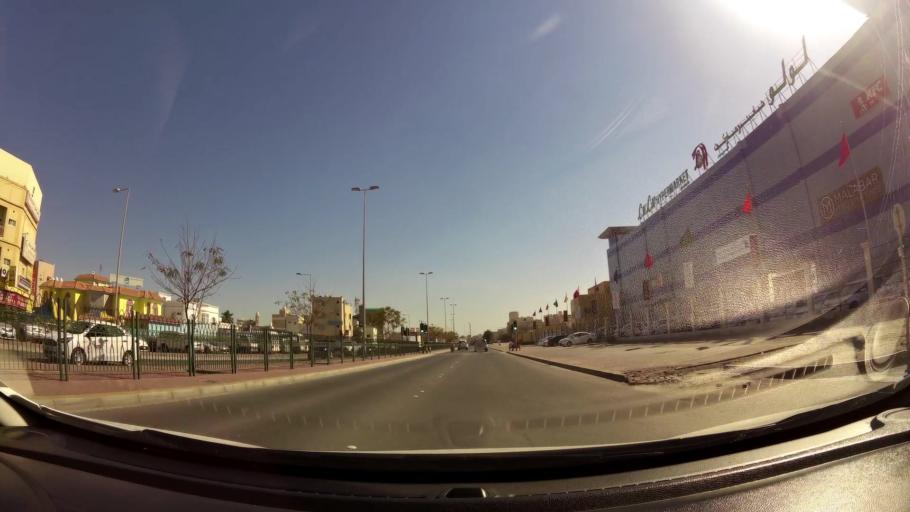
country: BH
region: Muharraq
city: Al Hadd
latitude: 26.2390
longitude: 50.6518
